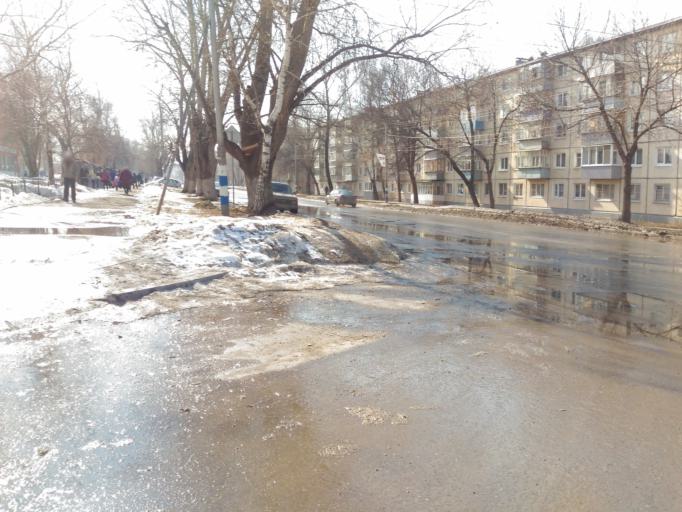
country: RU
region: Ulyanovsk
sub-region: Ulyanovskiy Rayon
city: Ulyanovsk
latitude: 54.3304
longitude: 48.4842
